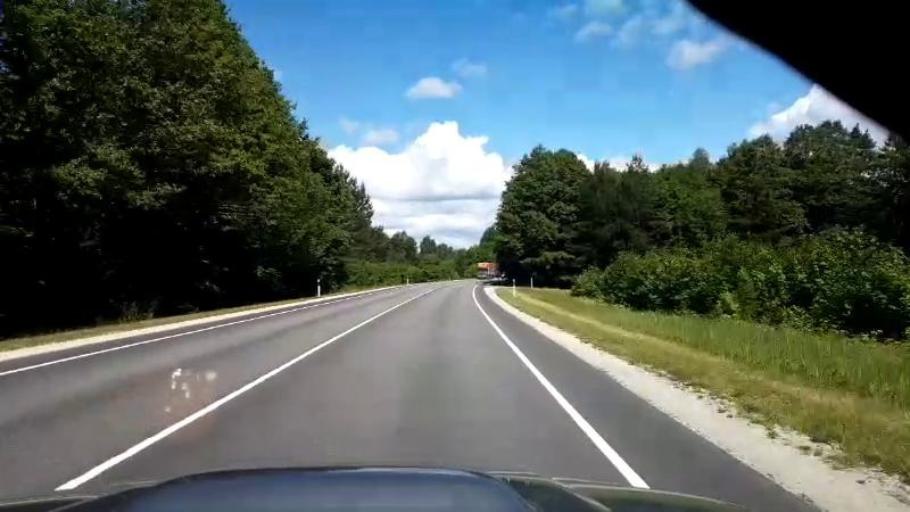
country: EE
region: Paernumaa
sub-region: Paernu linn
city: Parnu
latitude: 58.2264
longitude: 24.4948
